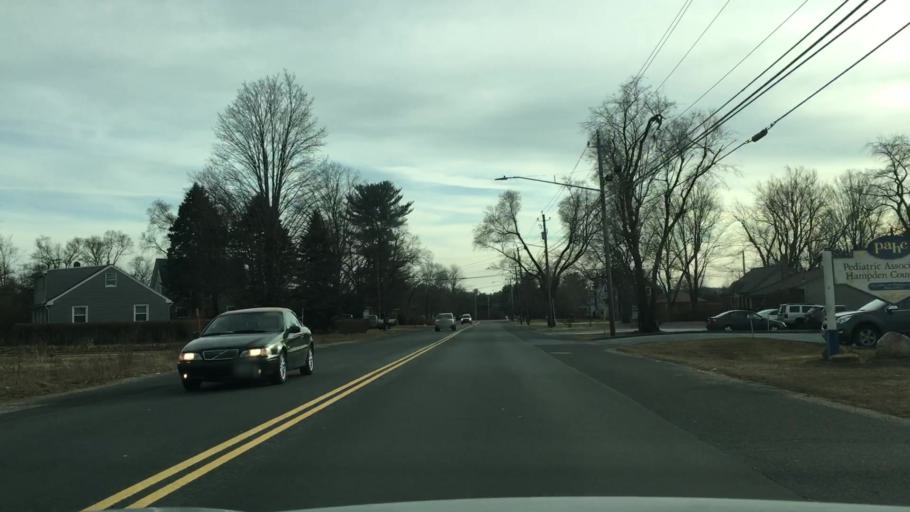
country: US
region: Massachusetts
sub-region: Hampden County
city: Westfield
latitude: 42.0940
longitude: -72.7630
